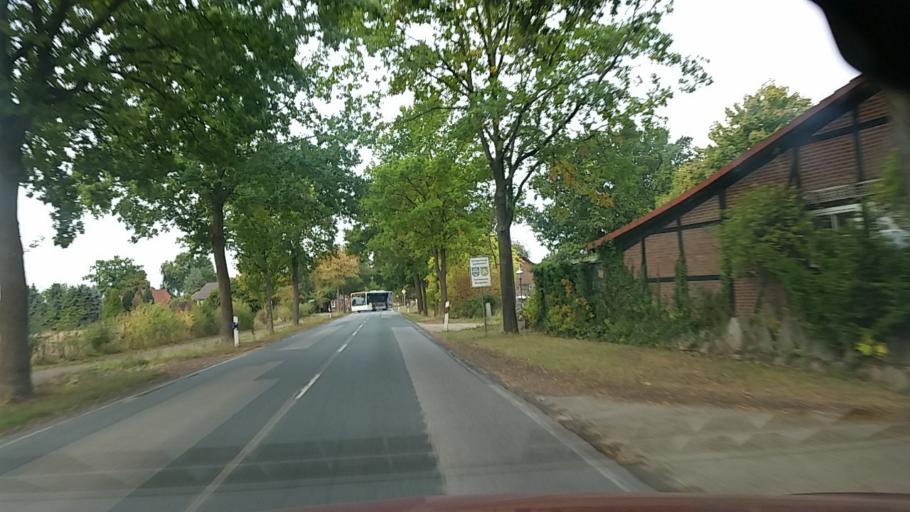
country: DE
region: Lower Saxony
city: Hohne
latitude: 52.5907
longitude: 10.3871
